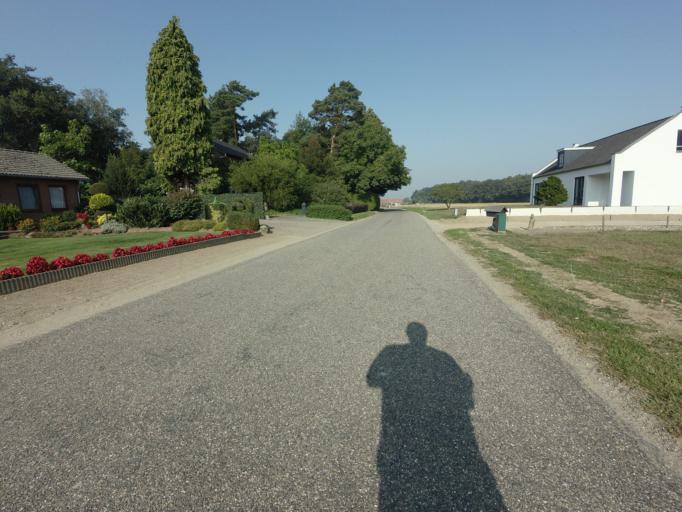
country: NL
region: Limburg
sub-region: Gemeente Beesel
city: Beesel
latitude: 51.2535
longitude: 6.0274
